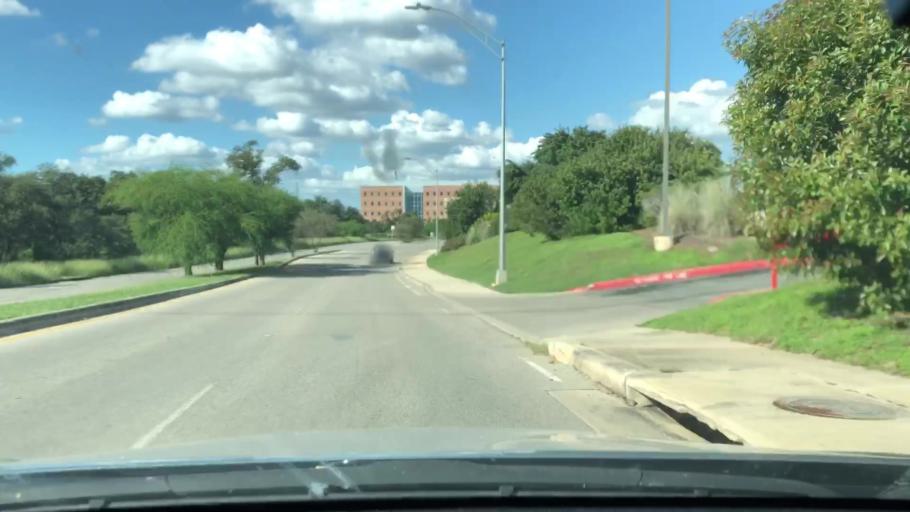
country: US
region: Texas
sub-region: Bexar County
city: Hollywood Park
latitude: 29.6128
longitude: -98.4784
